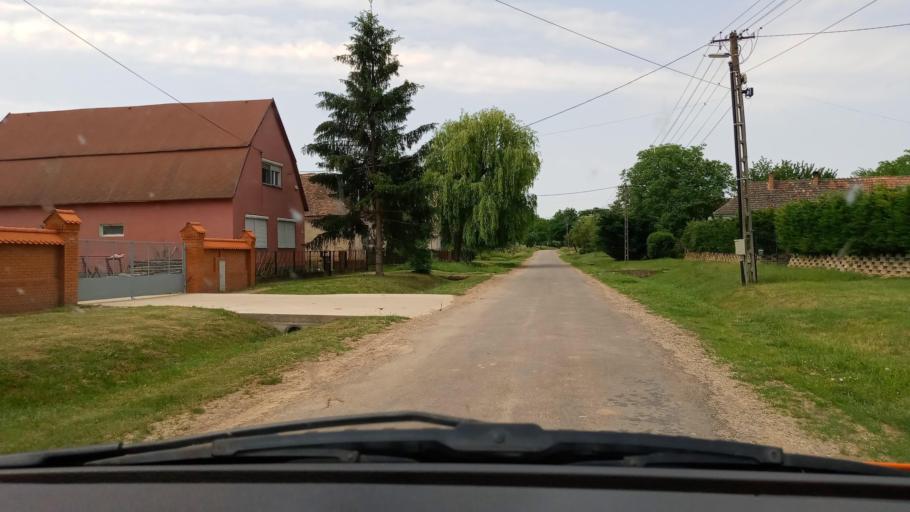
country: HU
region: Baranya
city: Szentlorinc
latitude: 45.9846
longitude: 18.0230
